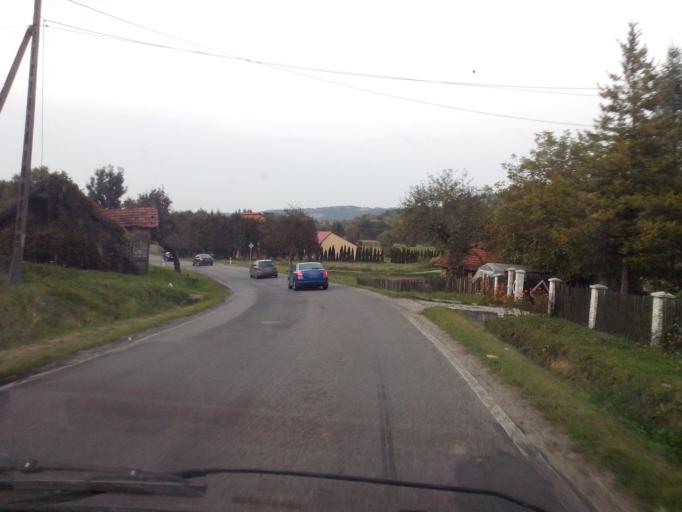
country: PL
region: Subcarpathian Voivodeship
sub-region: Powiat strzyzowski
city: Strzyzow
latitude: 49.8218
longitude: 21.8334
